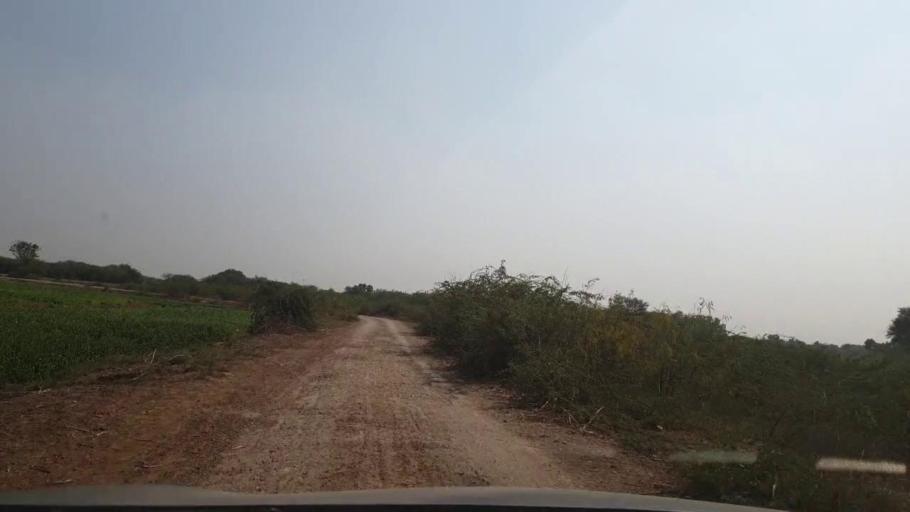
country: PK
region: Sindh
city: Tando Allahyar
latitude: 25.5578
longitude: 68.8444
